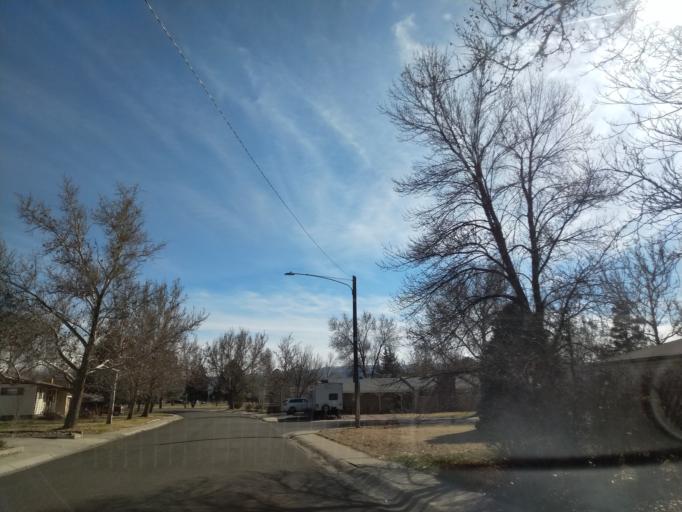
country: US
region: Colorado
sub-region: Mesa County
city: Grand Junction
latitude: 39.0841
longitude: -108.5674
